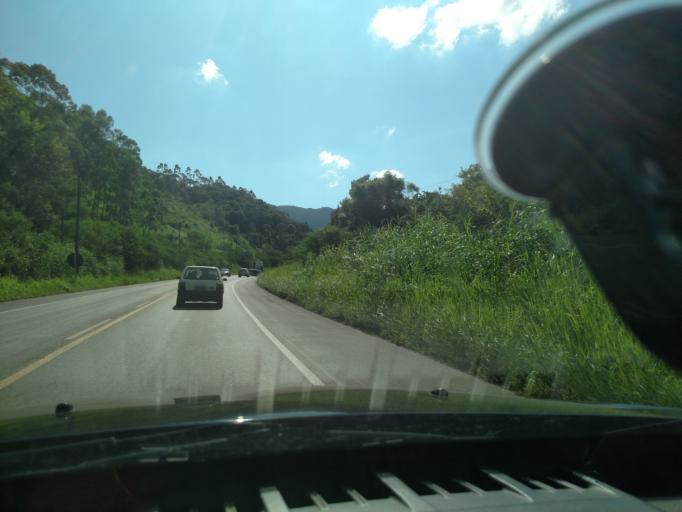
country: BR
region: Santa Catarina
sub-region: Ibirama
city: Ibirama
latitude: -27.0647
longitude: -49.4010
